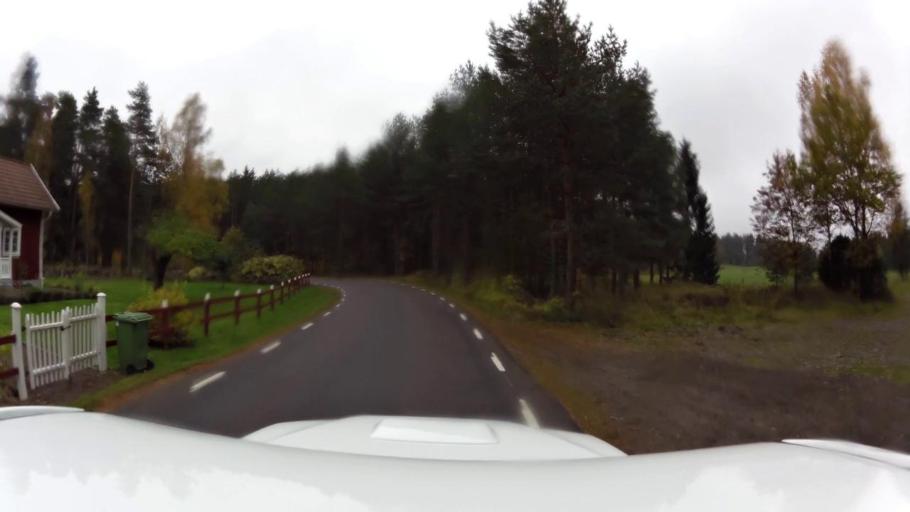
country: SE
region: OEstergoetland
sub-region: Linkopings Kommun
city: Linghem
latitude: 58.3564
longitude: 15.8475
